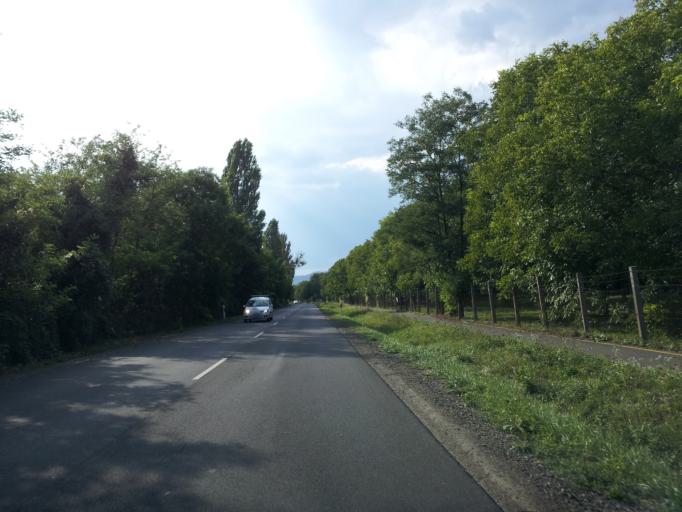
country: HU
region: Pest
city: Veroce
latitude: 47.8195
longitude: 19.0479
